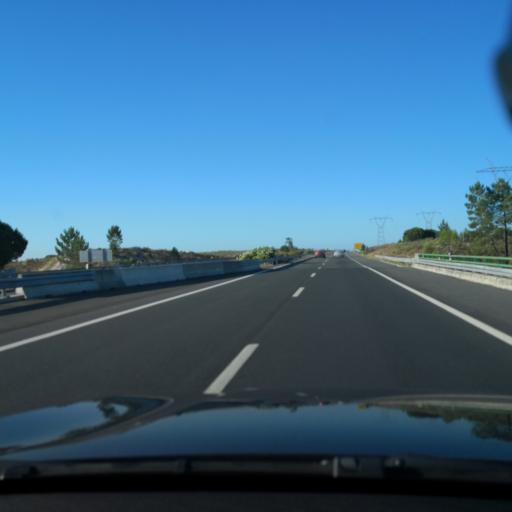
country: PT
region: Setubal
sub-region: Alcacer do Sal
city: Alcacer do Sal
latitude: 38.2940
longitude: -8.5091
